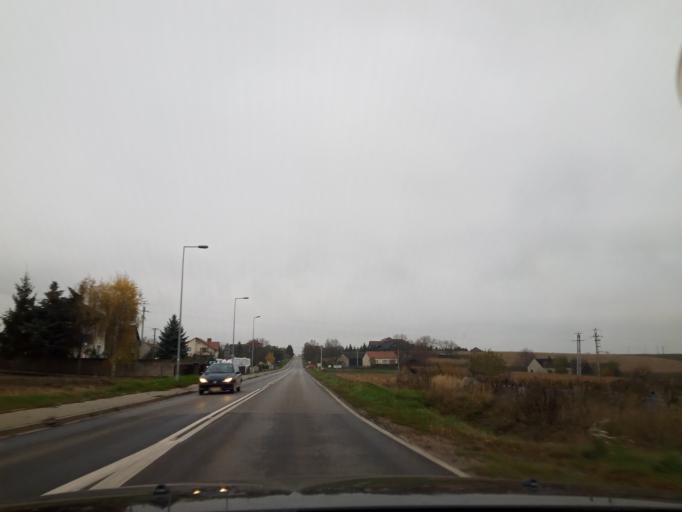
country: PL
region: Lesser Poland Voivodeship
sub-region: Powiat proszowicki
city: Proszowice
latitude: 50.2044
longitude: 20.3047
